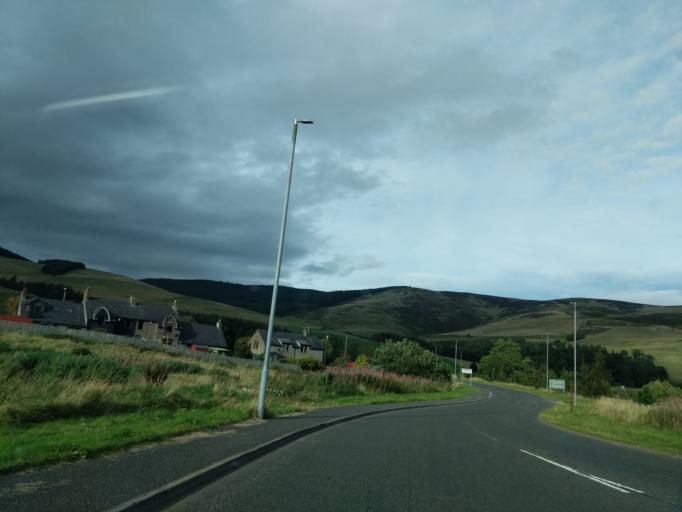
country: GB
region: Scotland
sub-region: The Scottish Borders
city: Innerleithen
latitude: 55.6410
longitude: -3.1160
